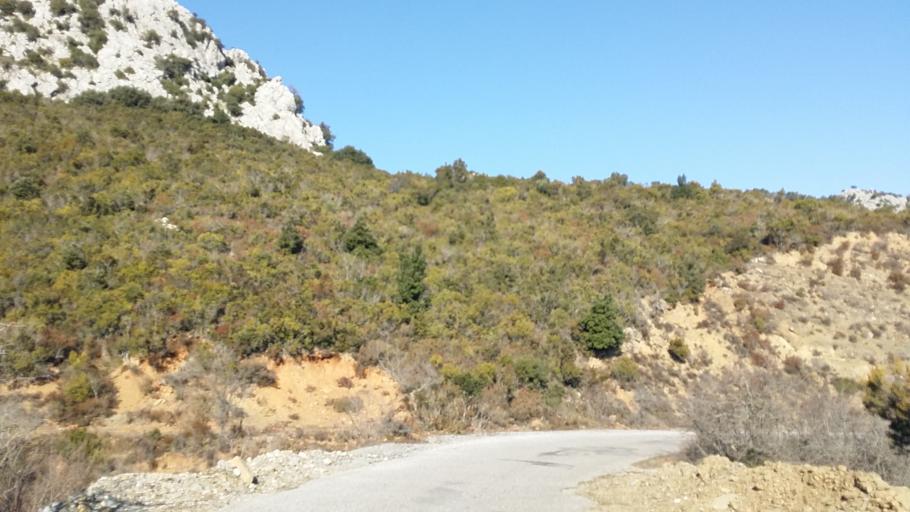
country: GR
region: West Greece
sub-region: Nomos Aitolias kai Akarnanias
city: Sardinia
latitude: 38.9243
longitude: 21.4243
